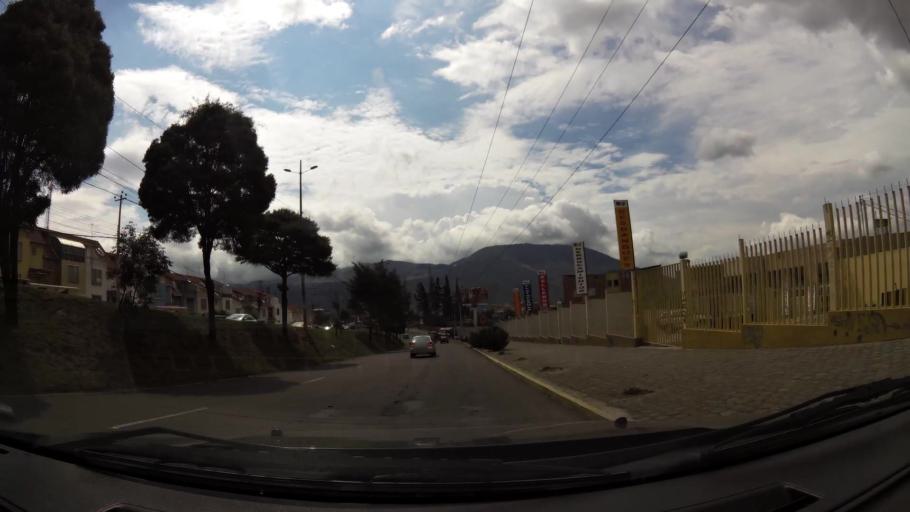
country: EC
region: Pichincha
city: Quito
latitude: -0.0936
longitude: -78.4709
